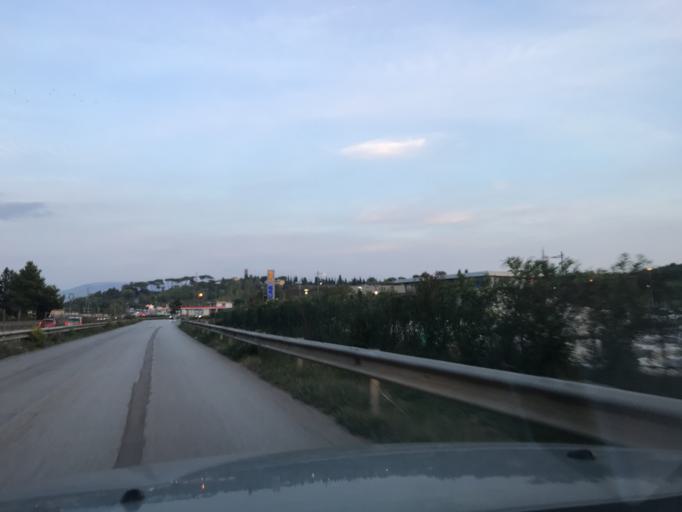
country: IT
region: Umbria
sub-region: Provincia di Perugia
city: Via Lippia
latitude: 43.0884
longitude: 12.4604
